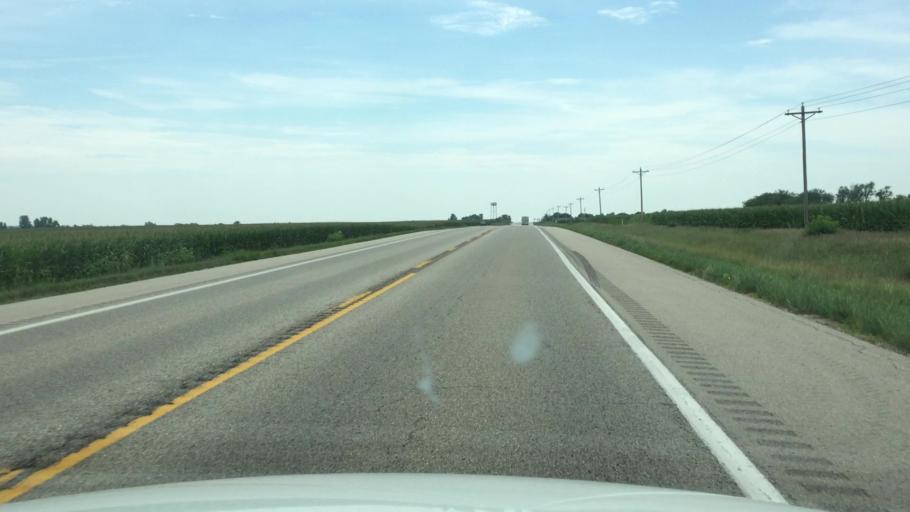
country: US
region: Kansas
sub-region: Nemaha County
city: Sabetha
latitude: 39.7153
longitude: -95.7300
